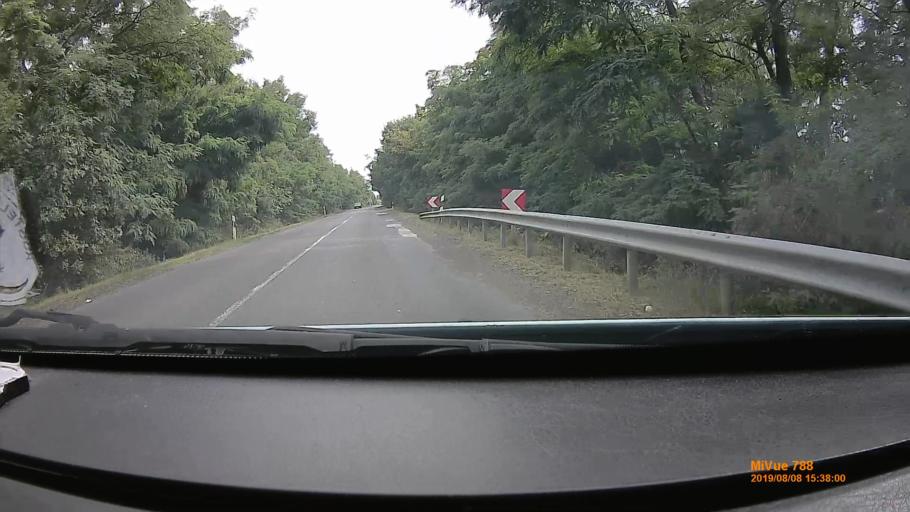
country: HU
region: Szabolcs-Szatmar-Bereg
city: Kocsord
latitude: 47.9461
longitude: 22.4271
